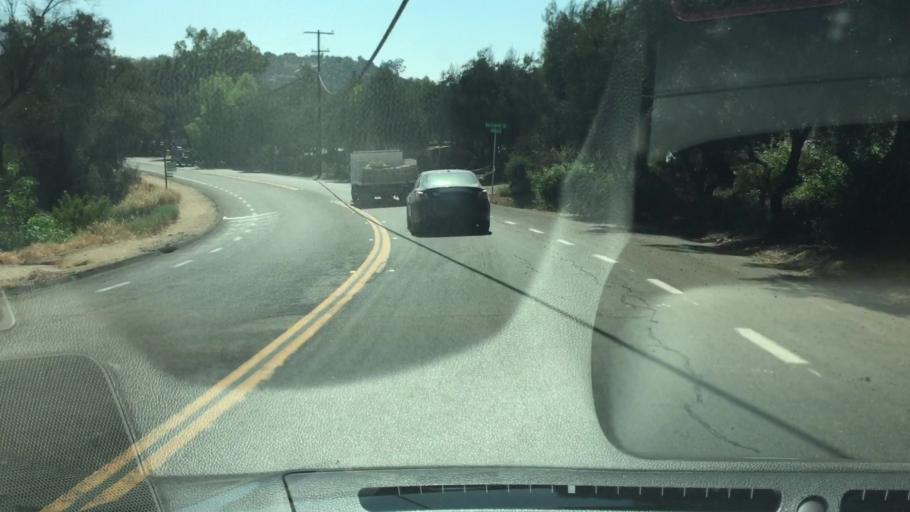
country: US
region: California
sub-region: San Diego County
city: Jamul
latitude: 32.7293
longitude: -116.8634
